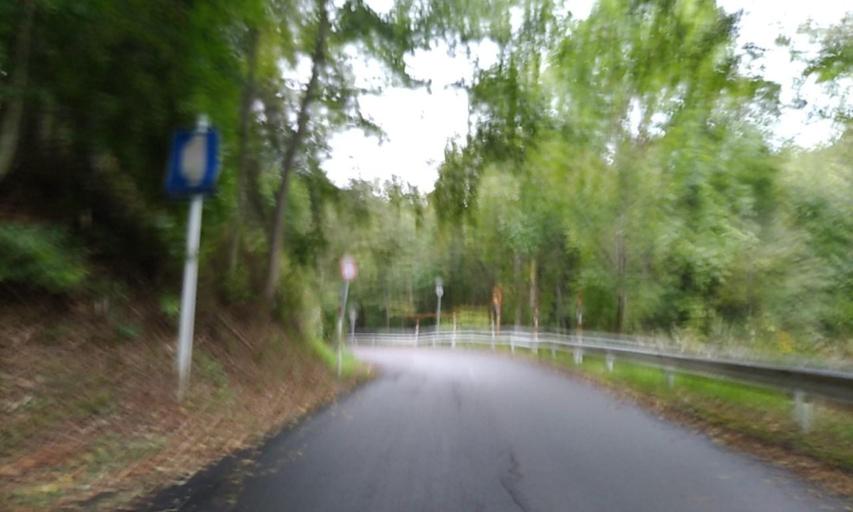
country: JP
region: Hokkaido
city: Bihoro
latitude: 43.5660
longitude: 144.1891
